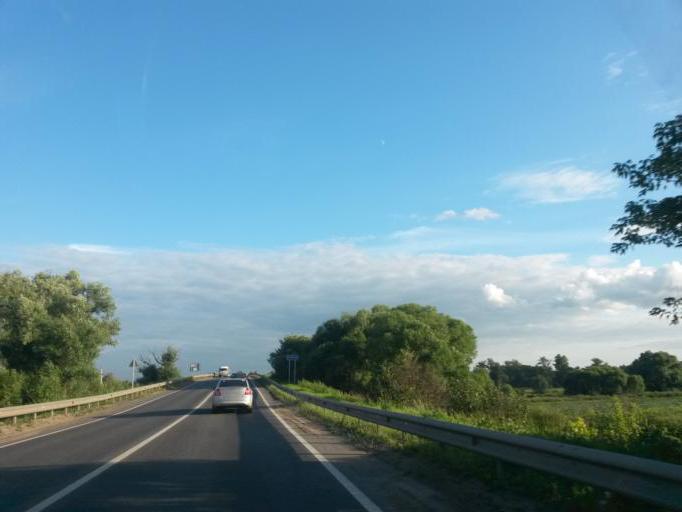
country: RU
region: Moskovskaya
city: Yam
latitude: 55.4946
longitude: 37.7503
